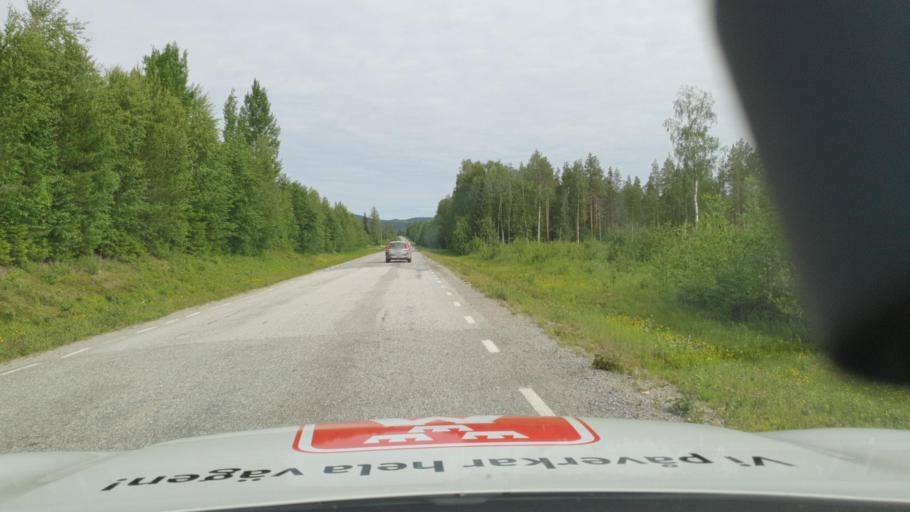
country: SE
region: Vaesterbotten
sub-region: Vindelns Kommun
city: Vindeln
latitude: 64.2097
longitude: 19.7643
